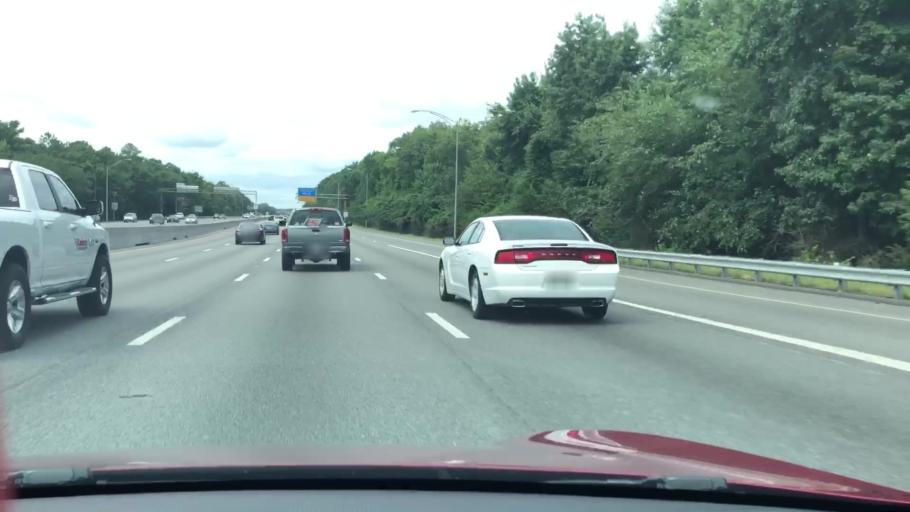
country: US
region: Virginia
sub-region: City of Virginia Beach
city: Virginia Beach
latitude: 36.8381
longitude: -76.1003
